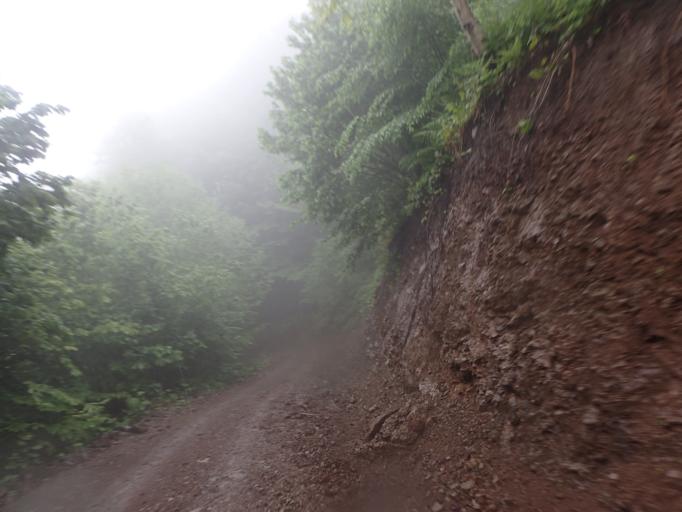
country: TR
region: Samsun
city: Salipazari
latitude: 40.9516
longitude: 36.8934
